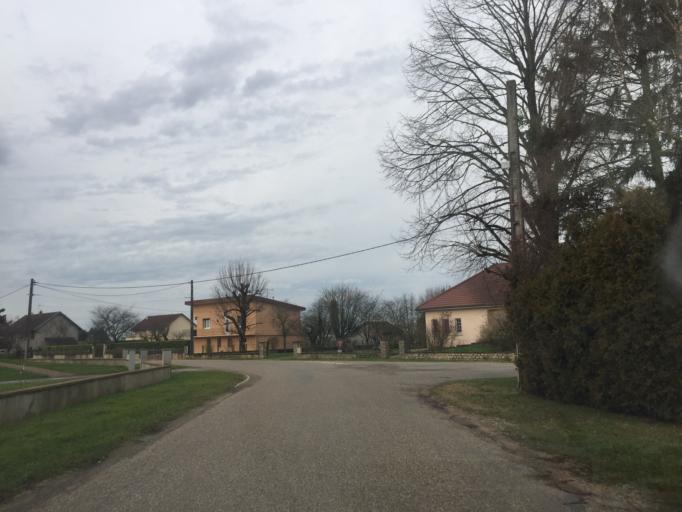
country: FR
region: Franche-Comte
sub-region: Departement du Jura
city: Tavaux
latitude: 47.0376
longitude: 5.4380
